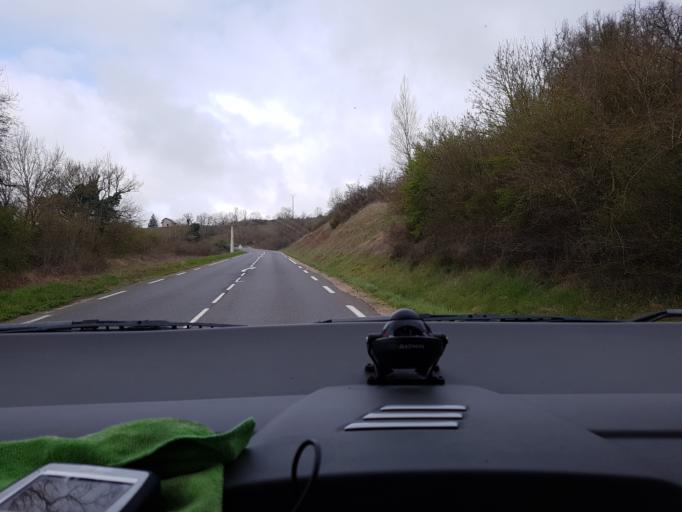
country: FR
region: Midi-Pyrenees
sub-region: Departement de l'Aveyron
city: Olemps
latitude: 44.3694
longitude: 2.5389
